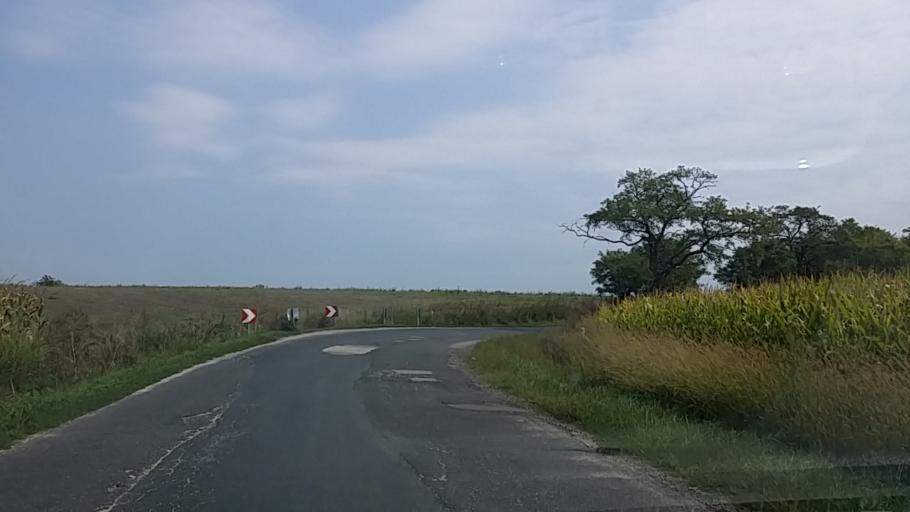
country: HU
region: Gyor-Moson-Sopron
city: Bosarkany
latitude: 47.6965
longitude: 17.2579
